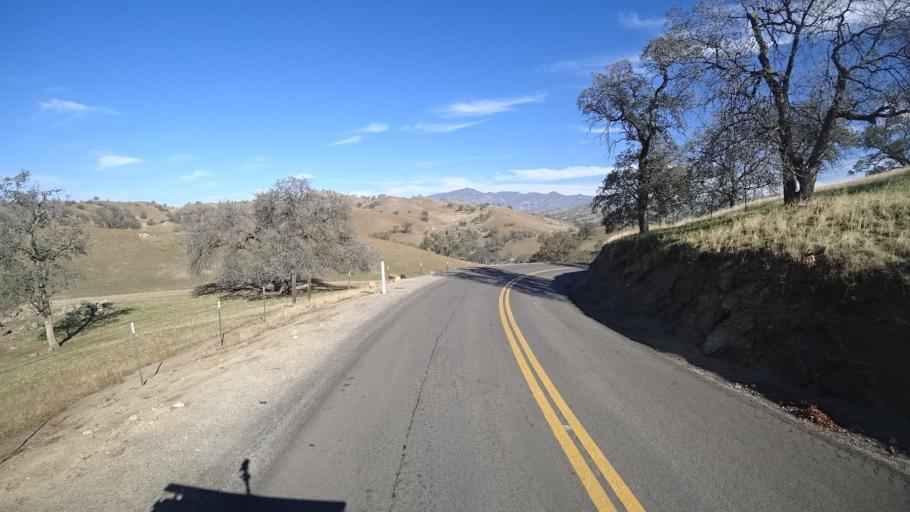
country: US
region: California
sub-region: Tulare County
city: Richgrove
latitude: 35.6986
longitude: -118.8583
